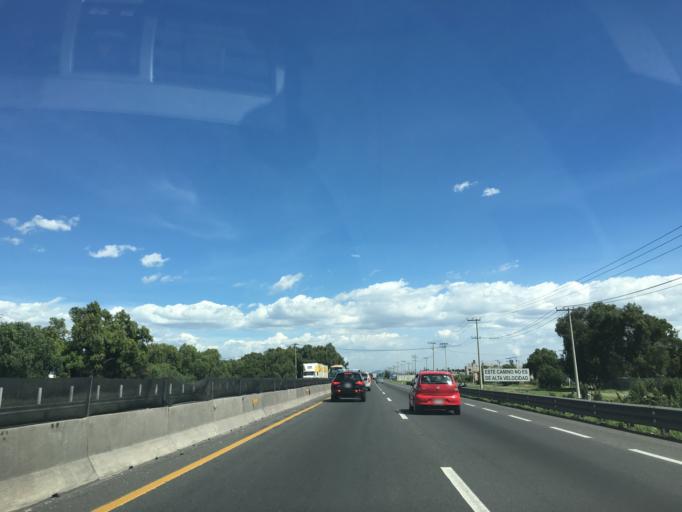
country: MX
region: Mexico
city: Ecatepec
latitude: 19.6319
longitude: -99.0500
